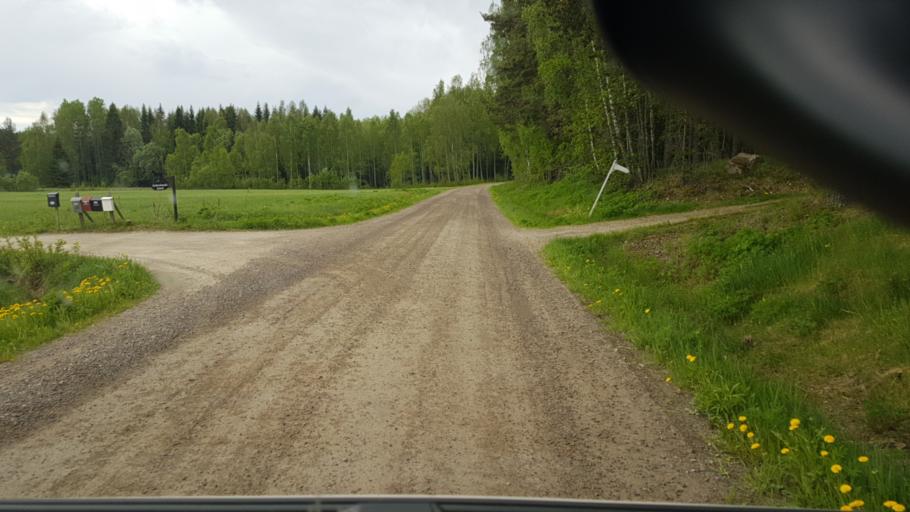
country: SE
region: Vaermland
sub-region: Arvika Kommun
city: Arvika
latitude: 59.5290
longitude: 12.7407
